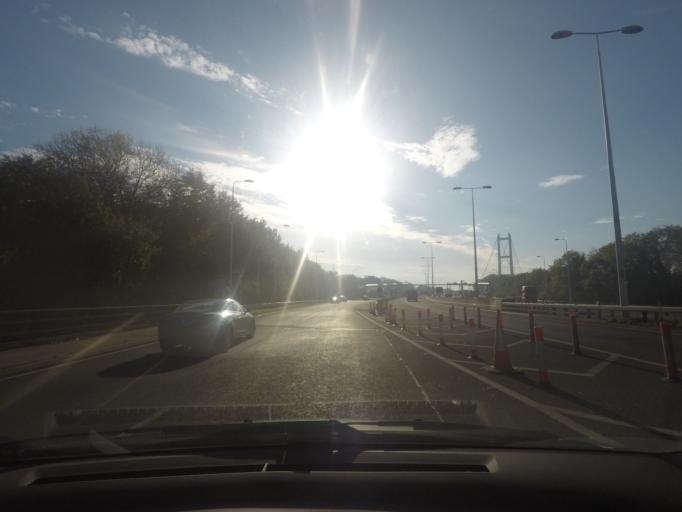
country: GB
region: England
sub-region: East Riding of Yorkshire
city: Hessle
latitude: 53.7217
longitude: -0.4523
